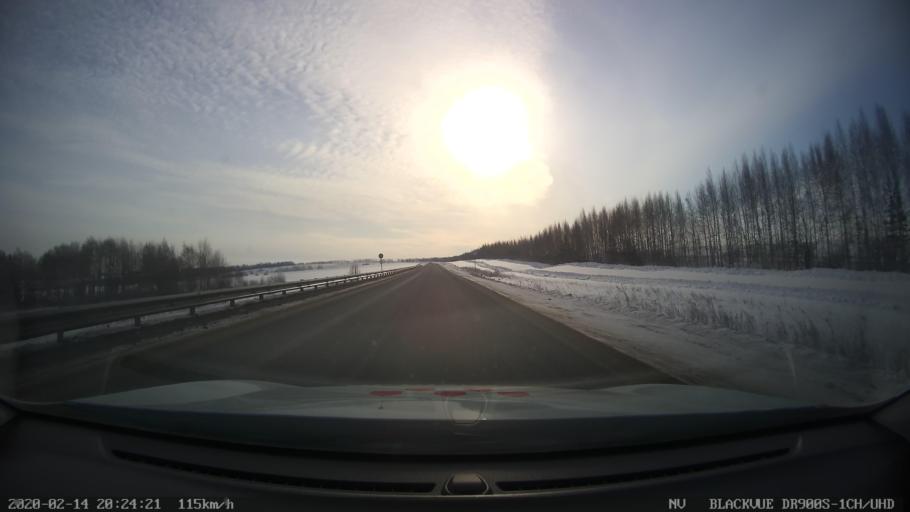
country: RU
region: Tatarstan
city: Verkhniy Uslon
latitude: 55.5139
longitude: 48.9691
